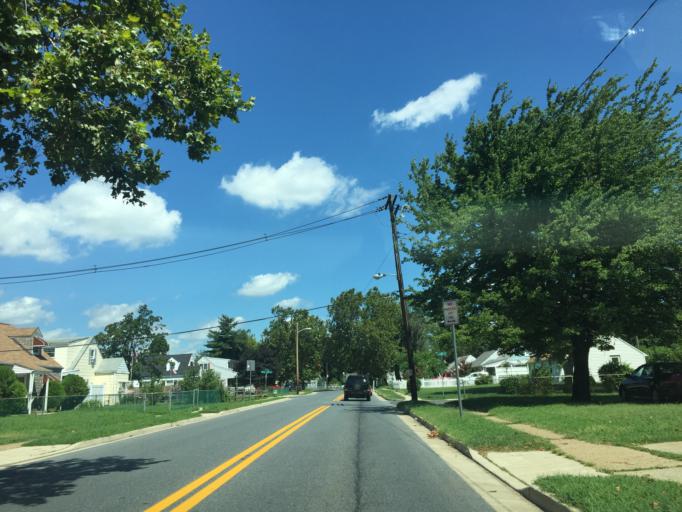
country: US
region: Maryland
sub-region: Baltimore County
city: Dundalk
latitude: 39.2507
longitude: -76.5095
